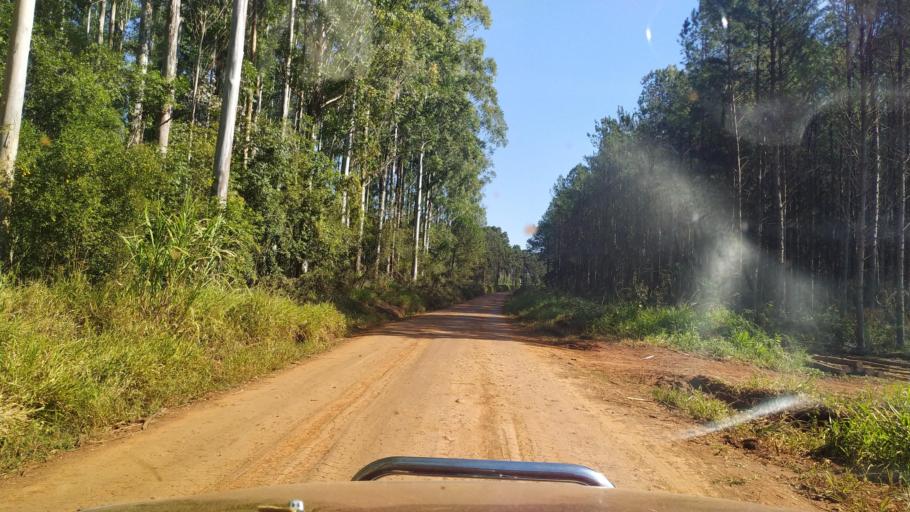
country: AR
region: Misiones
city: El Alcazar
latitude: -26.7155
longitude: -54.7078
